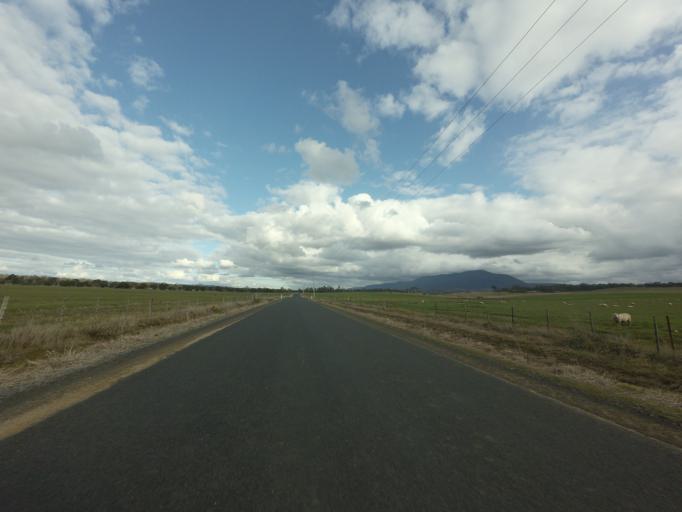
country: AU
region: Tasmania
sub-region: Northern Midlands
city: Longford
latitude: -41.8258
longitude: 147.2045
